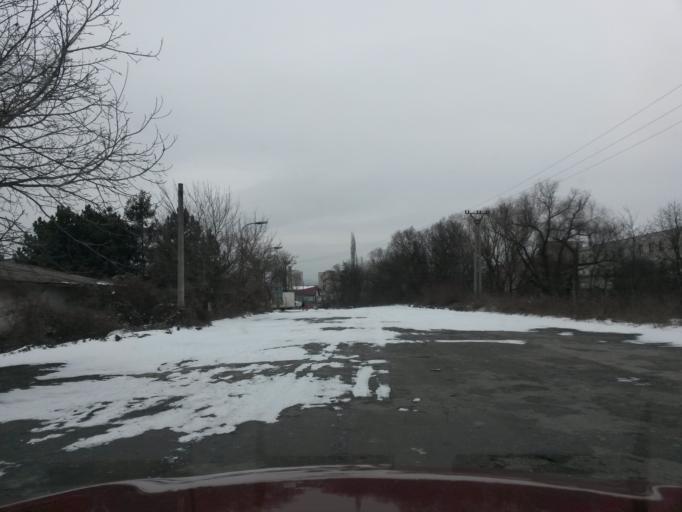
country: SK
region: Kosicky
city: Kosice
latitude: 48.7080
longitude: 21.2719
